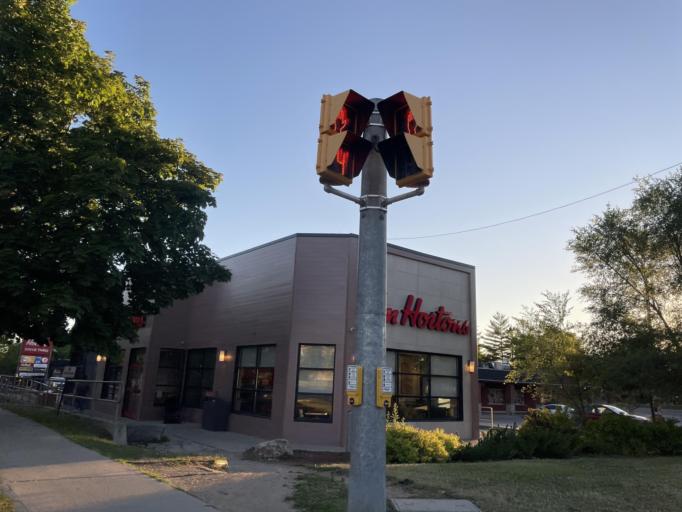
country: CA
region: Ontario
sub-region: Wellington County
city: Guelph
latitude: 43.5777
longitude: -80.2601
